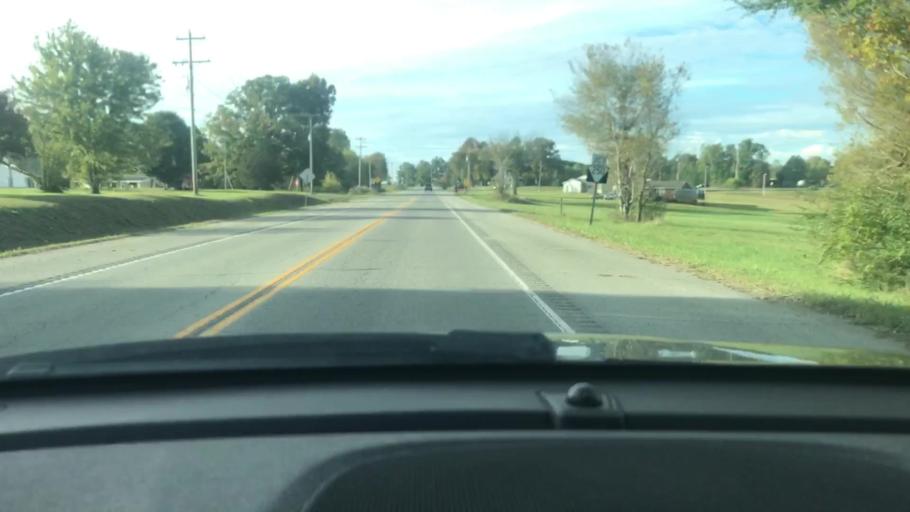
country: US
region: Tennessee
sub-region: Dickson County
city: White Bluff
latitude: 36.1357
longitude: -87.2376
